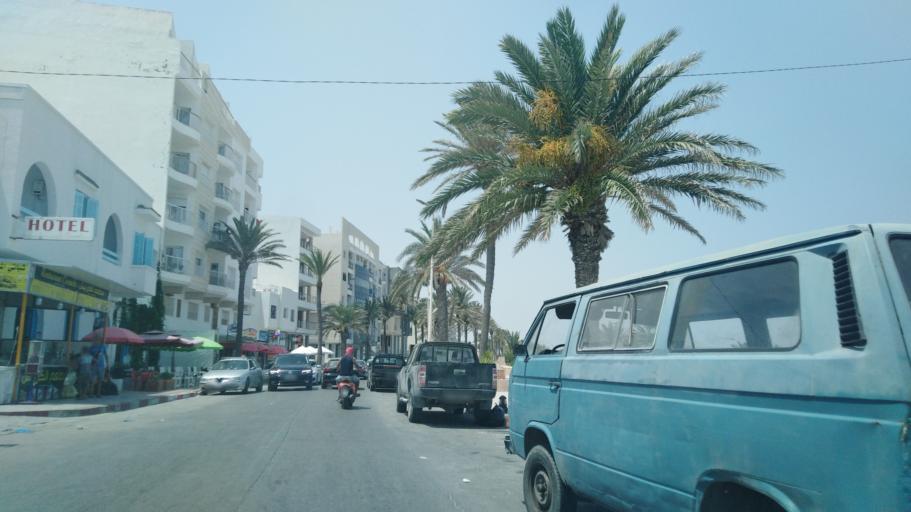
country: TN
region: Al Mahdiyah
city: Mahdia
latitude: 35.5097
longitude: 11.0548
